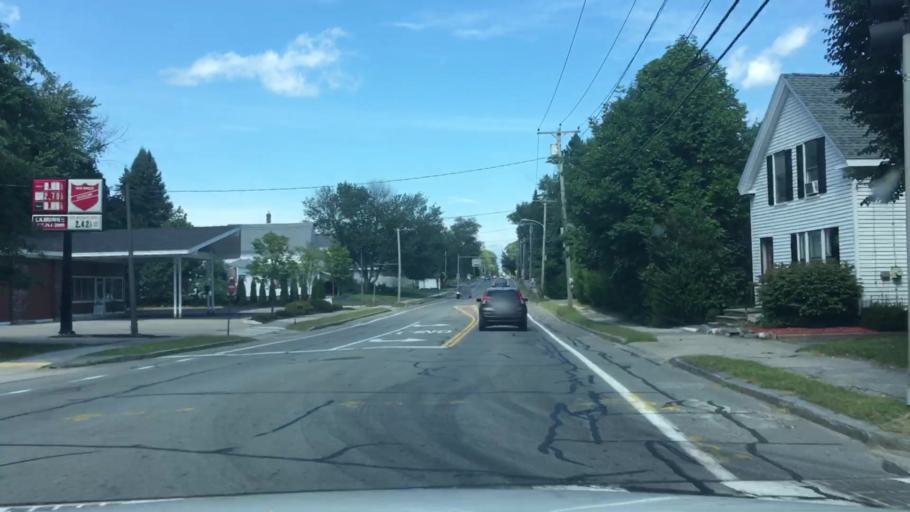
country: US
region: Maine
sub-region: Cumberland County
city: Falmouth
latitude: 43.7065
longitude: -70.2901
